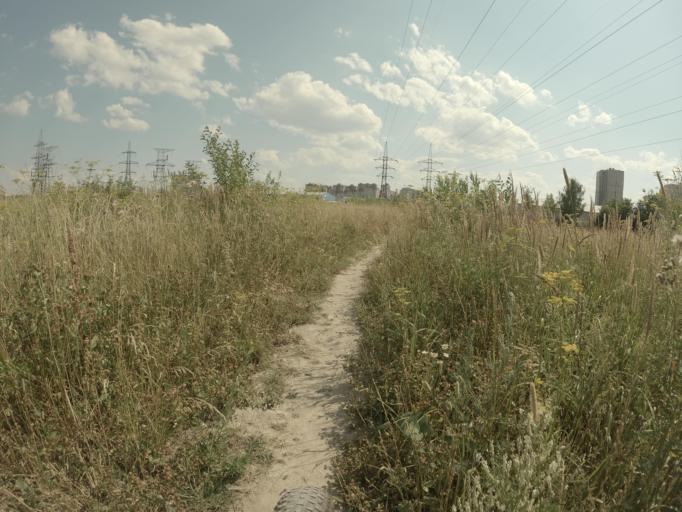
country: RU
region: St.-Petersburg
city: Kupchino
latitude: 59.8486
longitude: 30.3425
